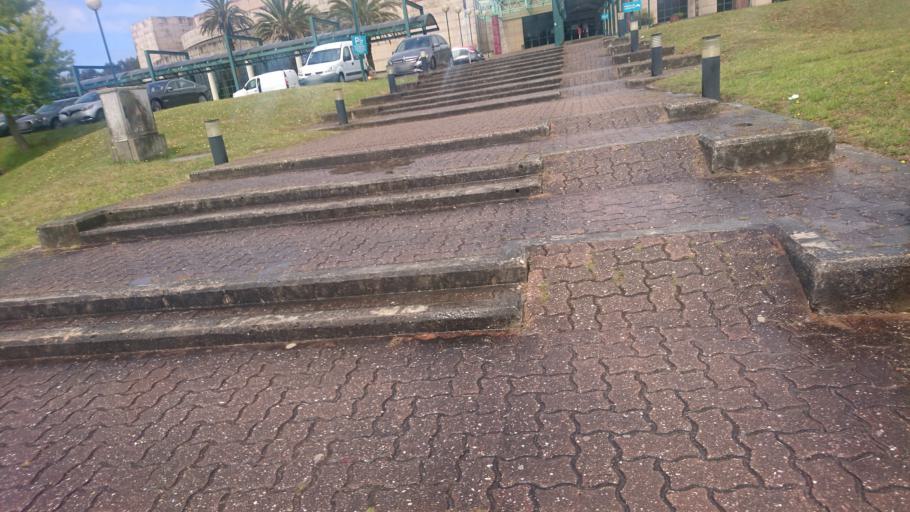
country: PT
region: Aveiro
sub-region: Santa Maria da Feira
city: Rio Meao
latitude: 40.9344
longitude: -8.5771
